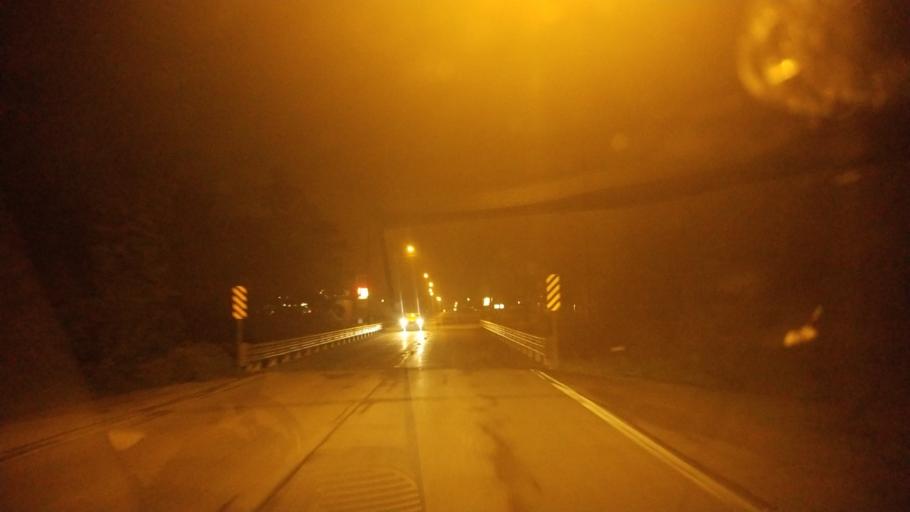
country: US
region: Missouri
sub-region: Pike County
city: Bowling Green
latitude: 39.3460
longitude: -91.2044
